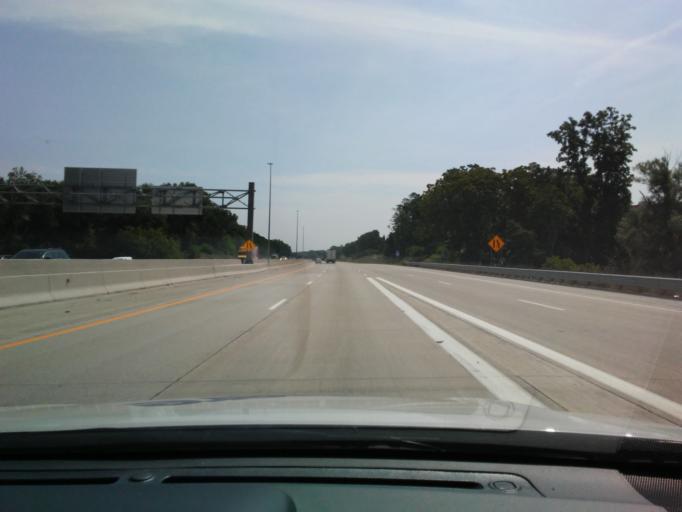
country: US
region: Michigan
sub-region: Livingston County
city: Brighton
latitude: 42.5223
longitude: -83.7453
